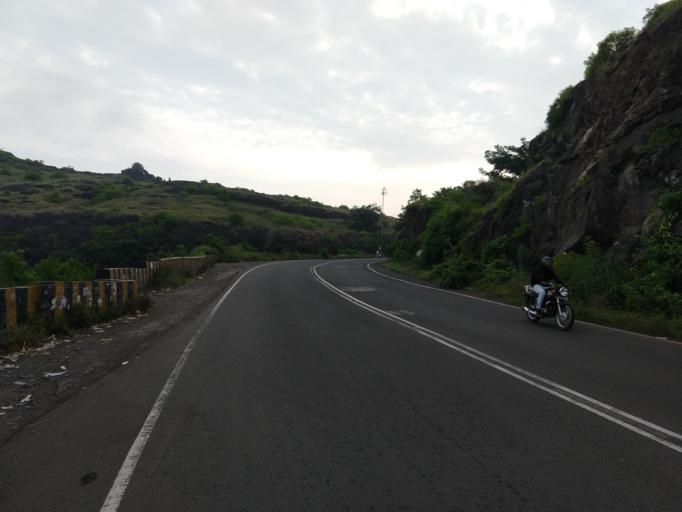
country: IN
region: Maharashtra
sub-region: Pune Division
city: Sasvad
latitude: 18.4159
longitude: 74.0037
